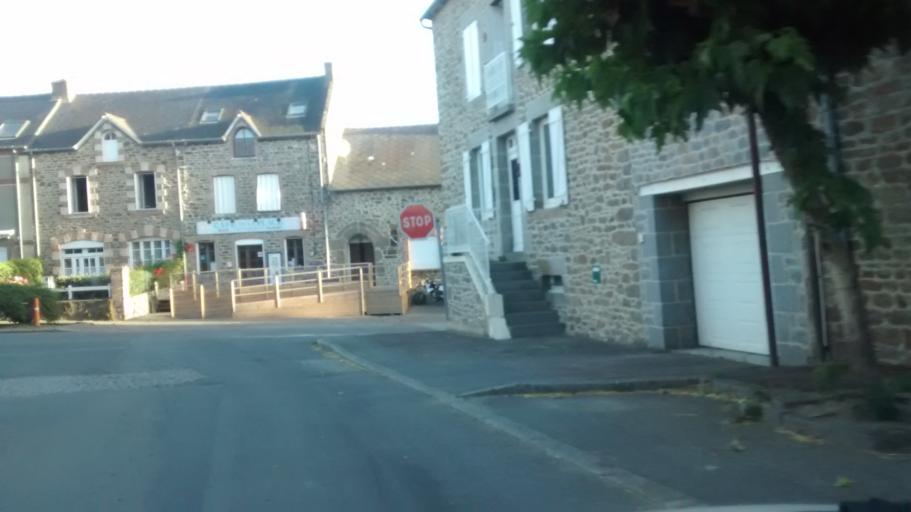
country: FR
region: Brittany
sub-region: Departement d'Ille-et-Vilaine
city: La Gouesniere
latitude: 48.5754
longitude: -1.8824
